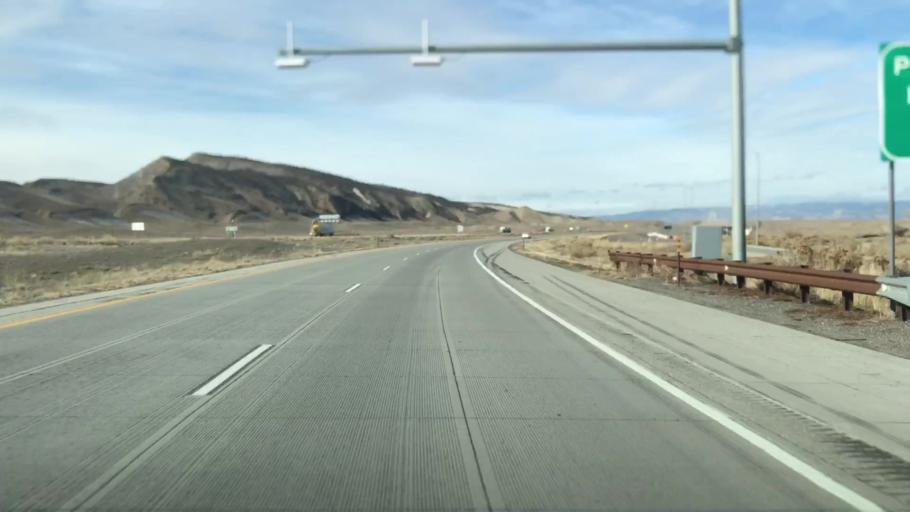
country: US
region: Colorado
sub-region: Mesa County
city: Loma
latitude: 39.1795
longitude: -108.8234
